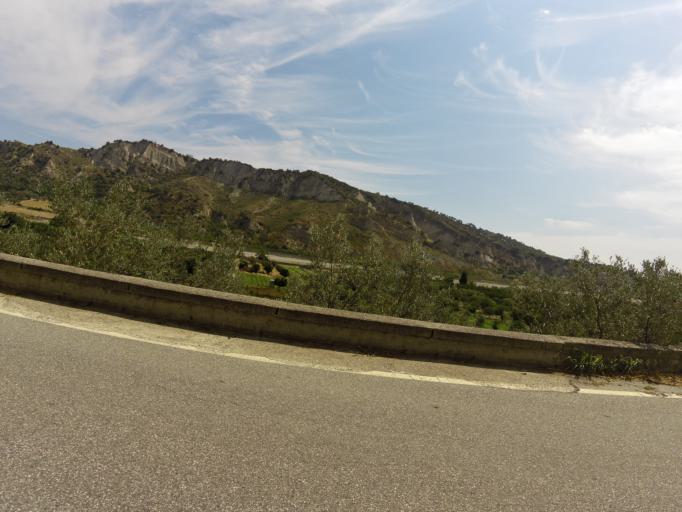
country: IT
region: Calabria
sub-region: Provincia di Reggio Calabria
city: Stilo
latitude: 38.4786
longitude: 16.4790
